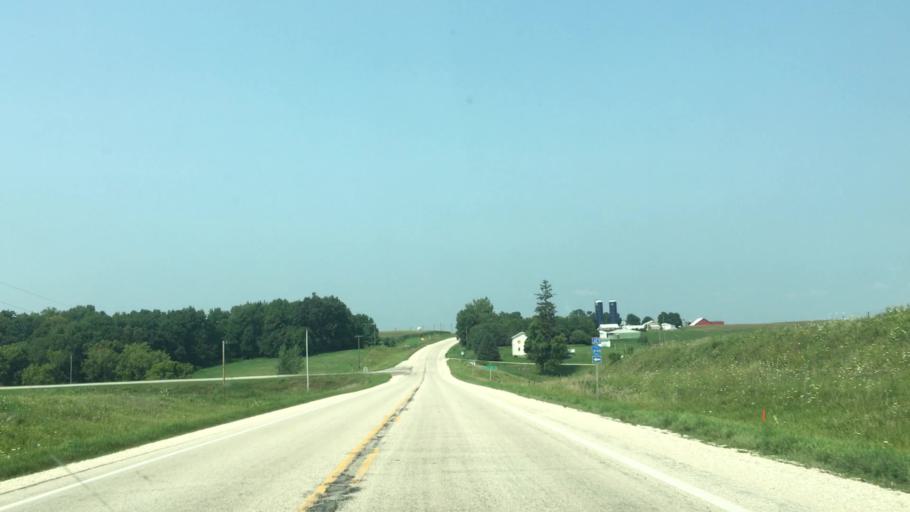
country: US
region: Iowa
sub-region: Fayette County
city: West Union
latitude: 43.0017
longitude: -91.8243
